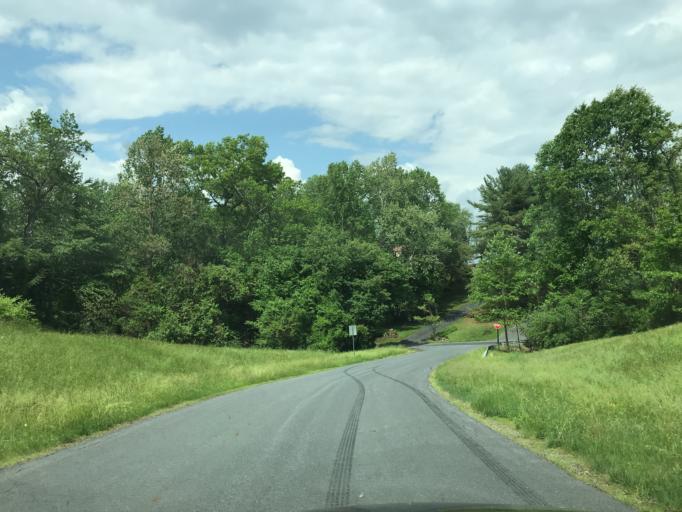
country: US
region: Maryland
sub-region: Harford County
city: Bel Air North
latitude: 39.5995
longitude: -76.3455
